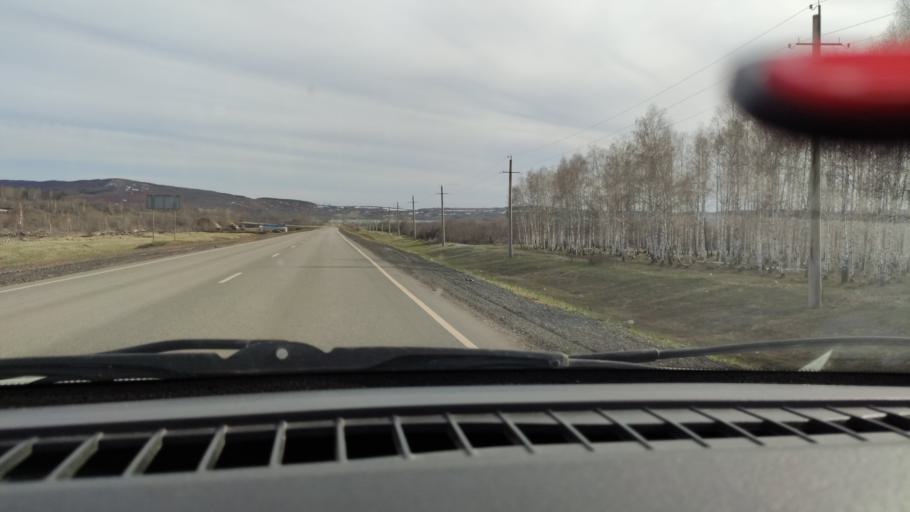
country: RU
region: Bashkortostan
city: Kumertau
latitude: 52.7789
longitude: 55.8592
